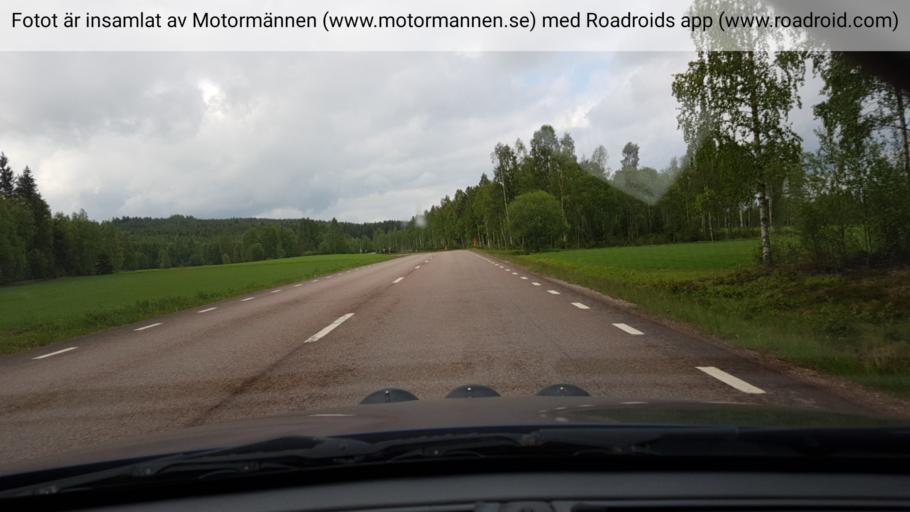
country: SE
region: Dalarna
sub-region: Orsa Kommun
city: Orsa
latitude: 61.1423
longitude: 14.6564
